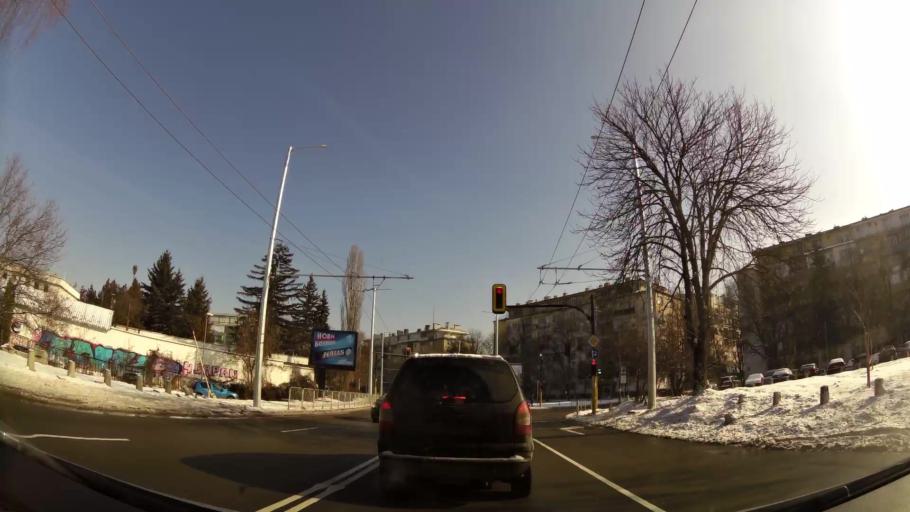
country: BG
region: Sofia-Capital
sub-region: Stolichna Obshtina
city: Sofia
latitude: 42.6742
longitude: 23.3115
